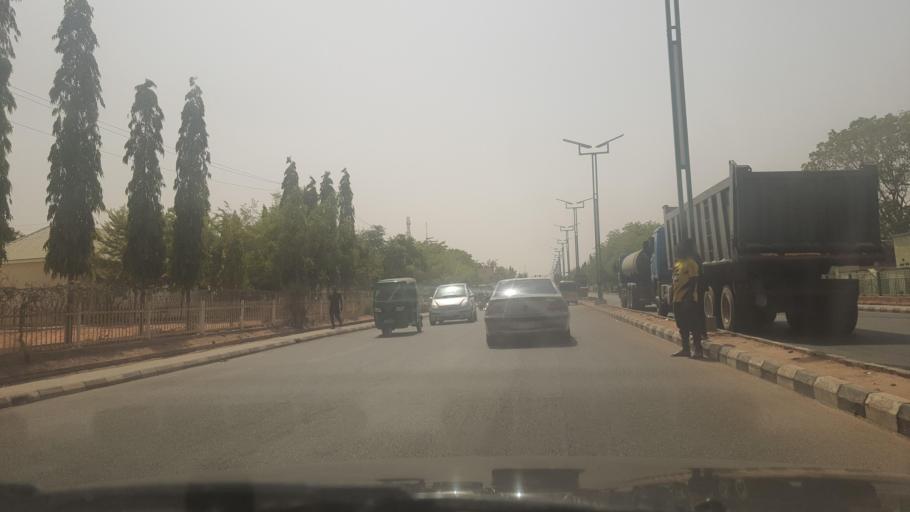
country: NG
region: Gombe
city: Gombe
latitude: 10.2841
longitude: 11.1500
